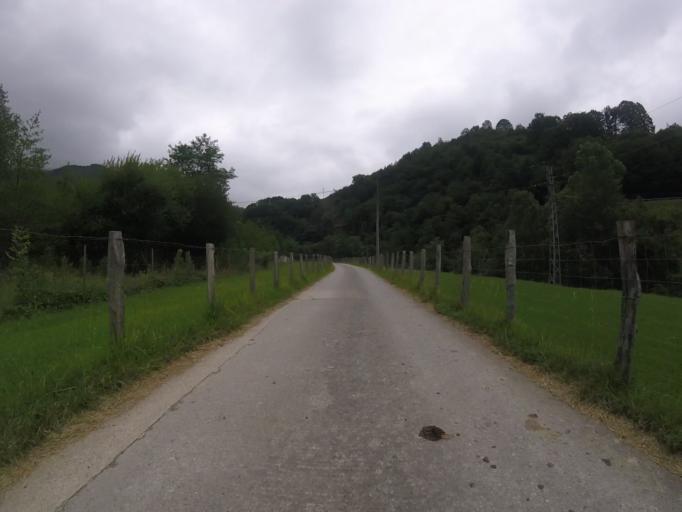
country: ES
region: Navarre
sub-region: Provincia de Navarra
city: Sunbilla
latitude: 43.1845
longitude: -1.6699
